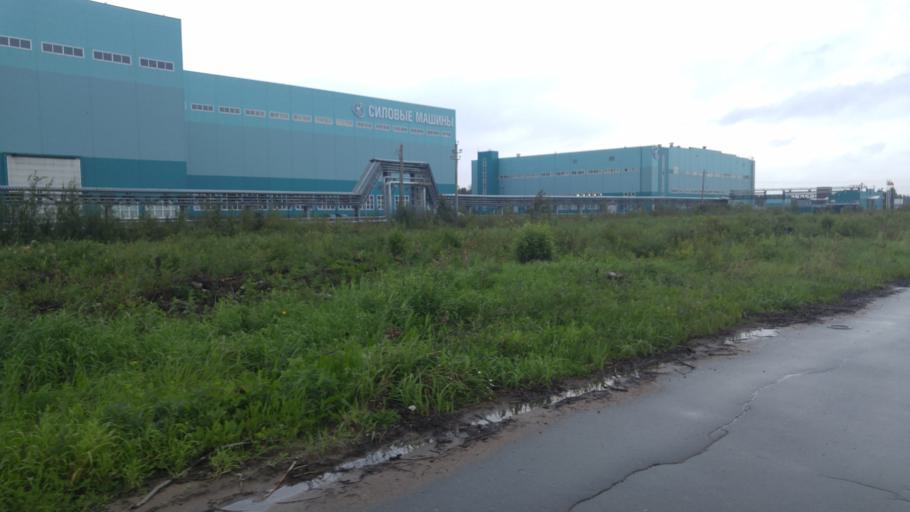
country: RU
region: St.-Petersburg
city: Metallostroy
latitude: 59.7789
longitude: 30.5643
